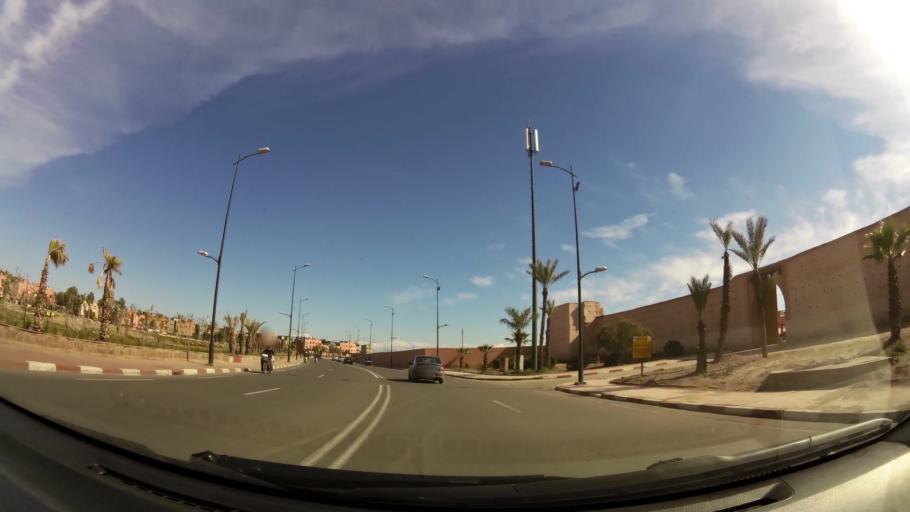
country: MA
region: Marrakech-Tensift-Al Haouz
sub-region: Marrakech
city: Marrakesh
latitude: 31.6372
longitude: -7.9804
